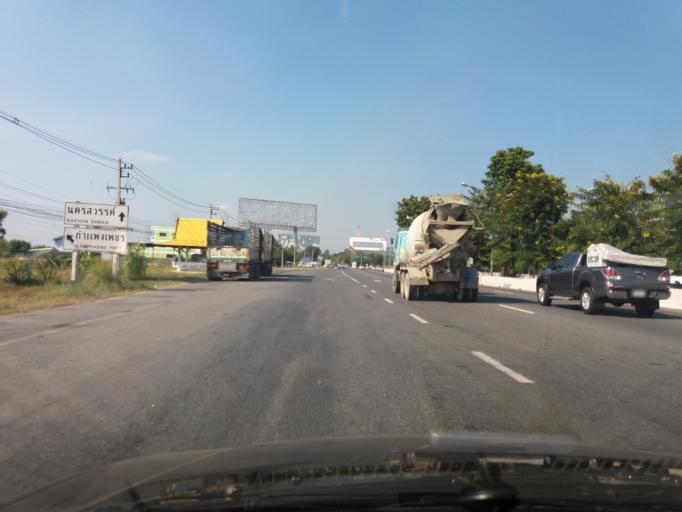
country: TH
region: Nakhon Sawan
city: Krok Phra
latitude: 15.6120
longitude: 100.1211
